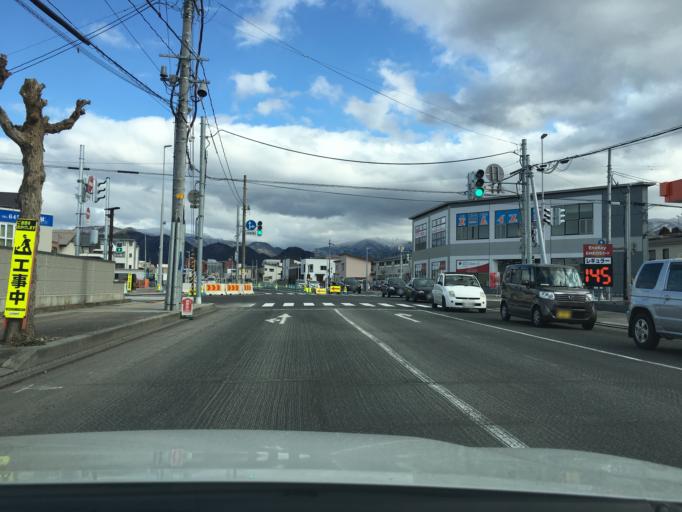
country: JP
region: Yamagata
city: Yamagata-shi
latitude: 38.2601
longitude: 140.3249
